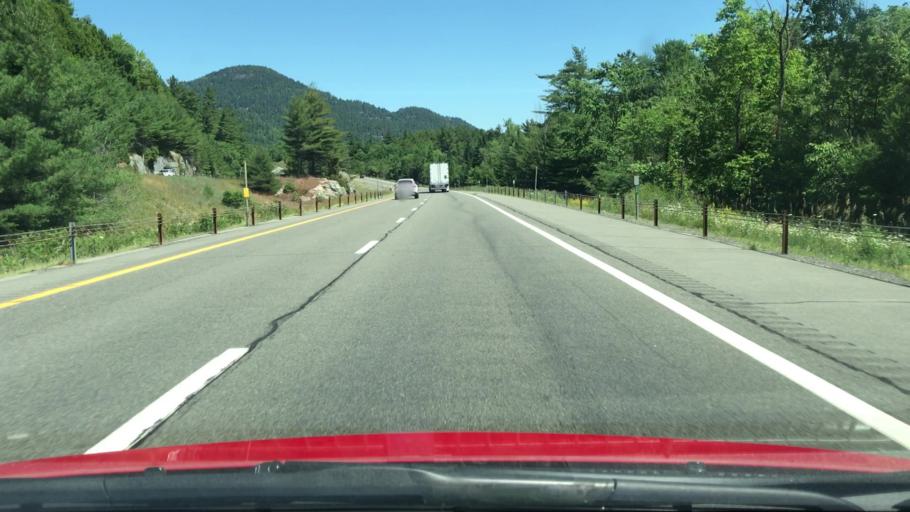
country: US
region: New York
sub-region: Essex County
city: Mineville
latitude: 43.9798
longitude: -73.7236
